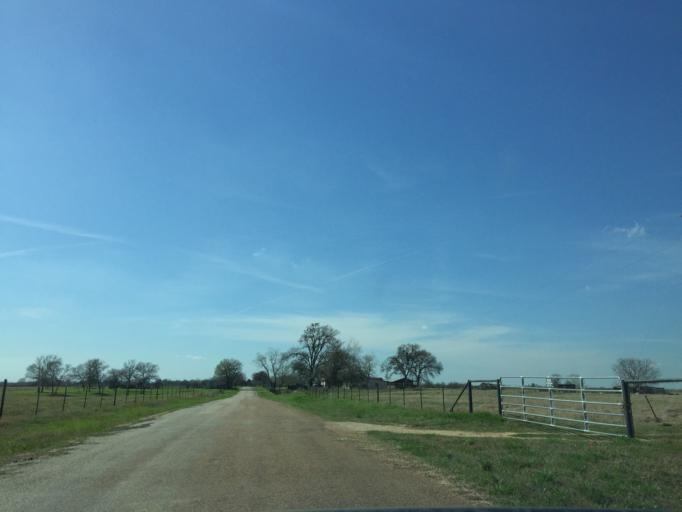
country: US
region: Texas
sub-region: Milam County
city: Thorndale
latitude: 30.5779
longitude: -97.1756
